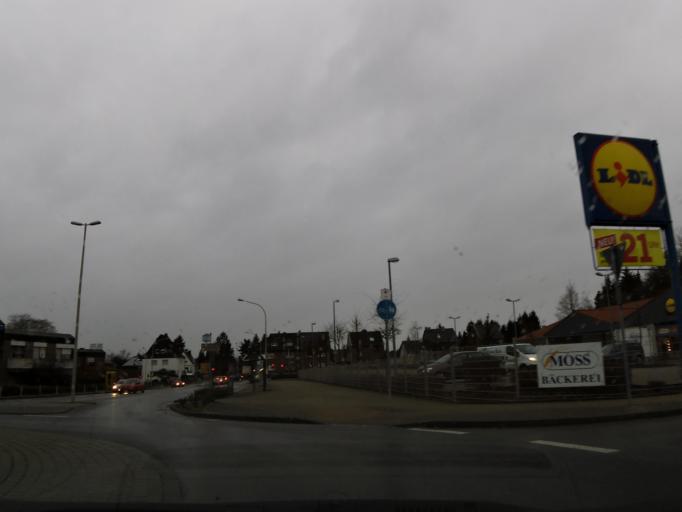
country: DE
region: North Rhine-Westphalia
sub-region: Regierungsbezirk Koln
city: Herzogenrath
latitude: 50.8708
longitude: 6.1029
